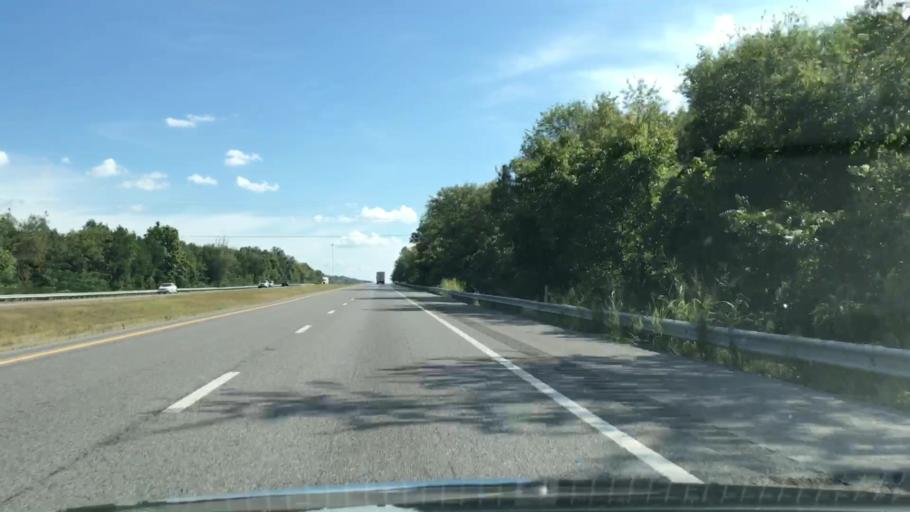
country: US
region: Alabama
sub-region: Limestone County
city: Ardmore
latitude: 35.0478
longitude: -86.8804
